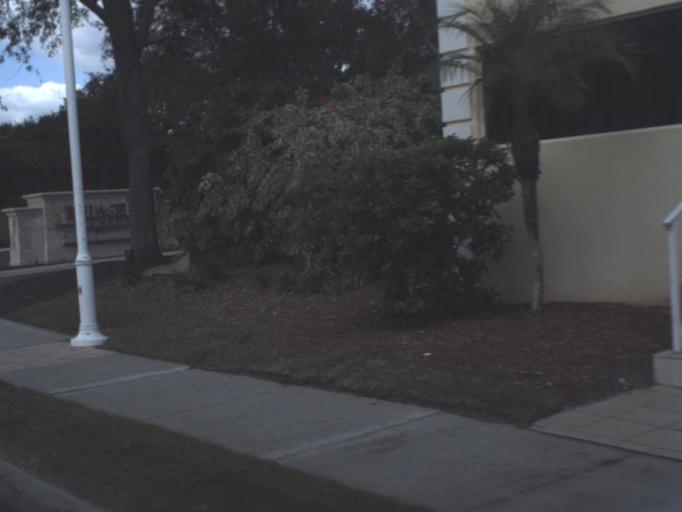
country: US
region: Florida
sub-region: Collier County
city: Naples
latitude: 26.1450
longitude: -81.7951
